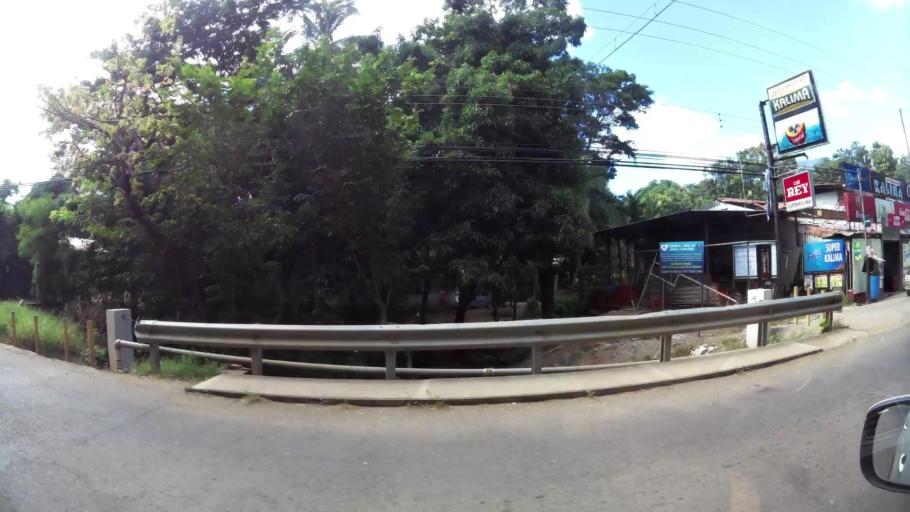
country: CR
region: Guanacaste
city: Santa Cruz
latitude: 10.3078
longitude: -85.8077
